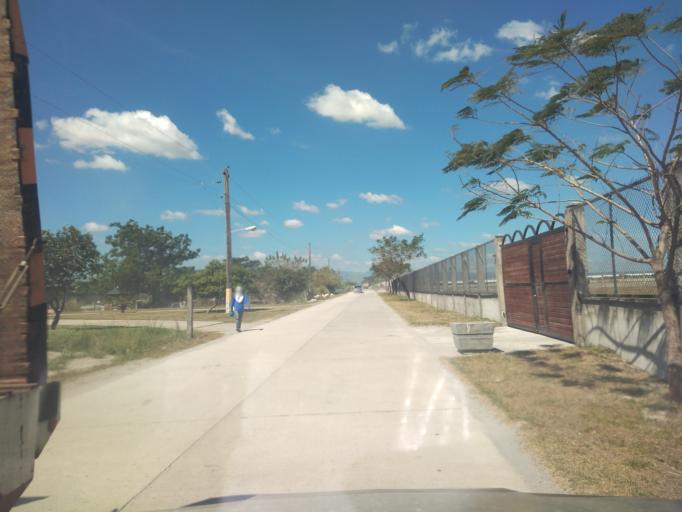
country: PH
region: Central Luzon
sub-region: Province of Pampanga
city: Balas
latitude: 15.0555
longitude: 120.6026
